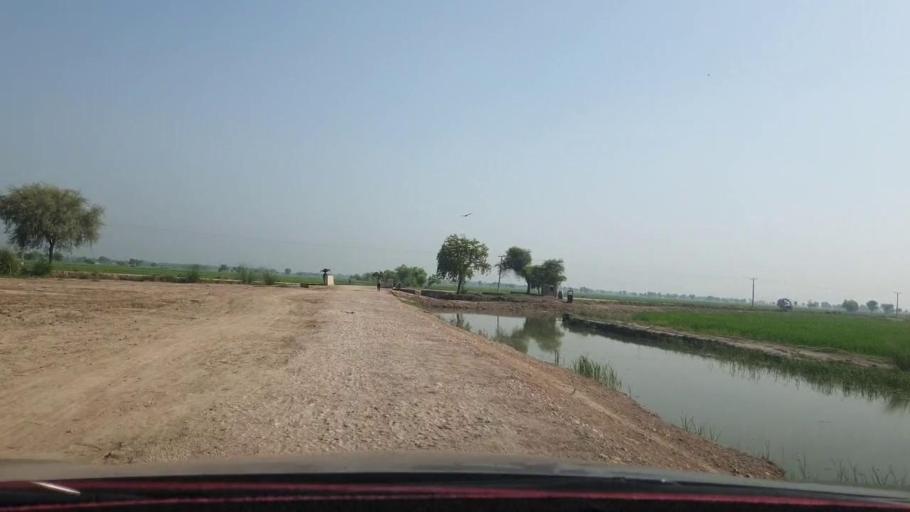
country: PK
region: Sindh
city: Kambar
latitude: 27.4968
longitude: 67.9309
